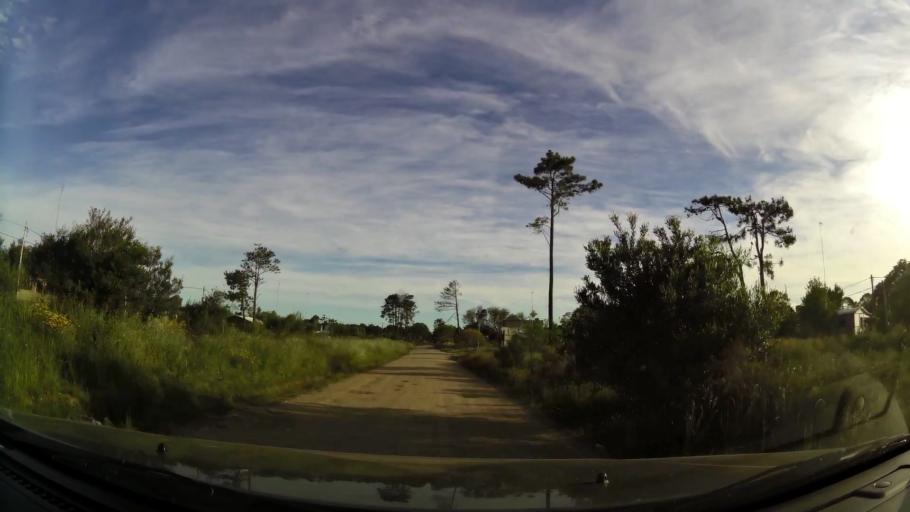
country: UY
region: Canelones
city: Empalme Olmos
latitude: -34.7736
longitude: -55.8643
